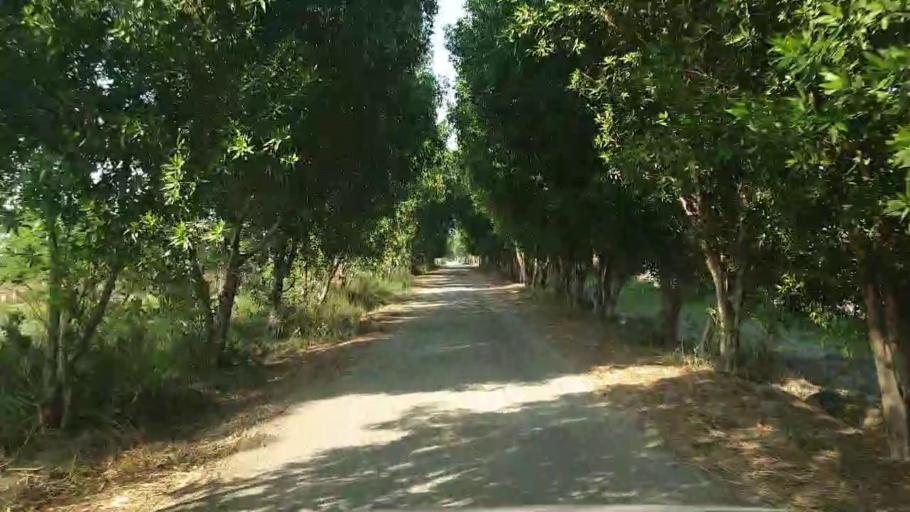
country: PK
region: Sindh
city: Badin
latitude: 24.6254
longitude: 68.8148
